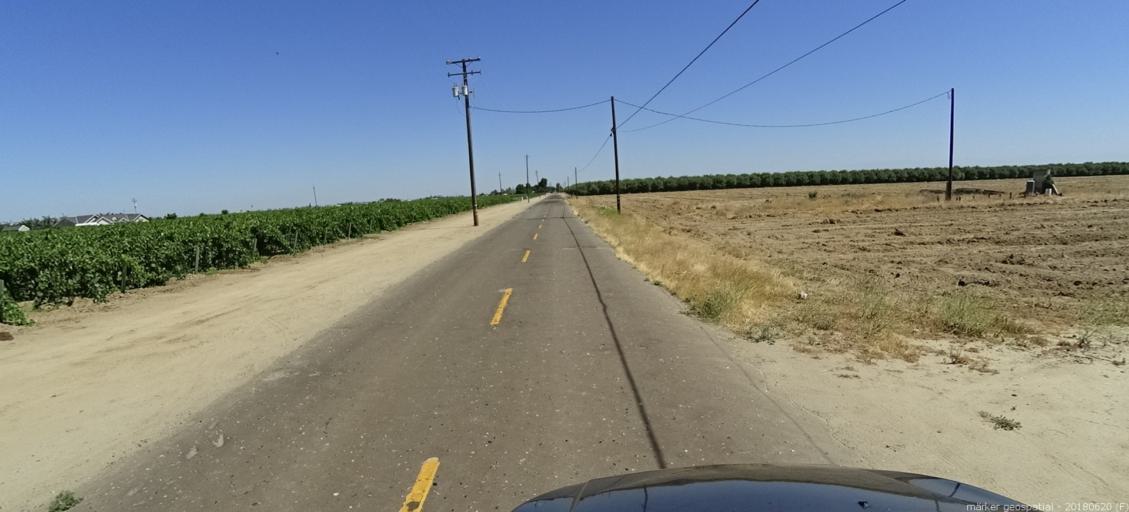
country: US
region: California
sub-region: Fresno County
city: Biola
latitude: 36.8530
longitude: -120.0102
